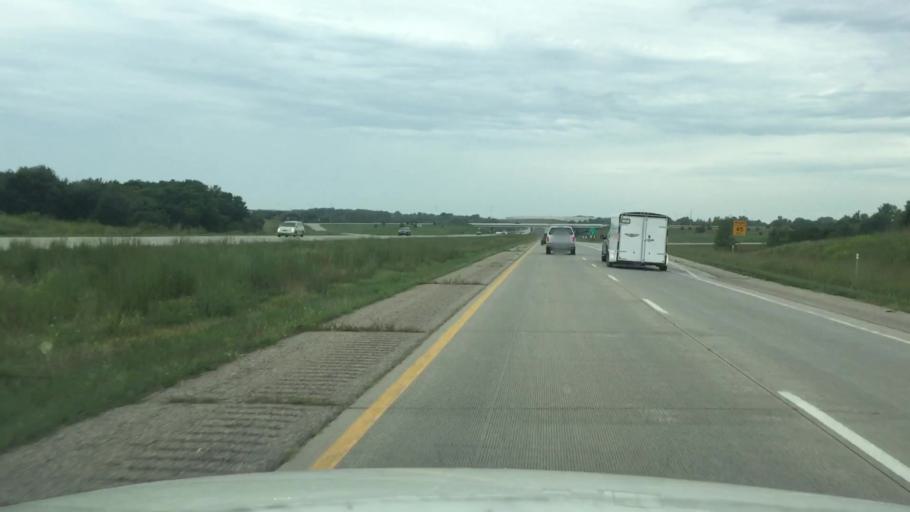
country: US
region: Iowa
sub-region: Warren County
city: Norwalk
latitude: 41.5042
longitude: -93.6374
